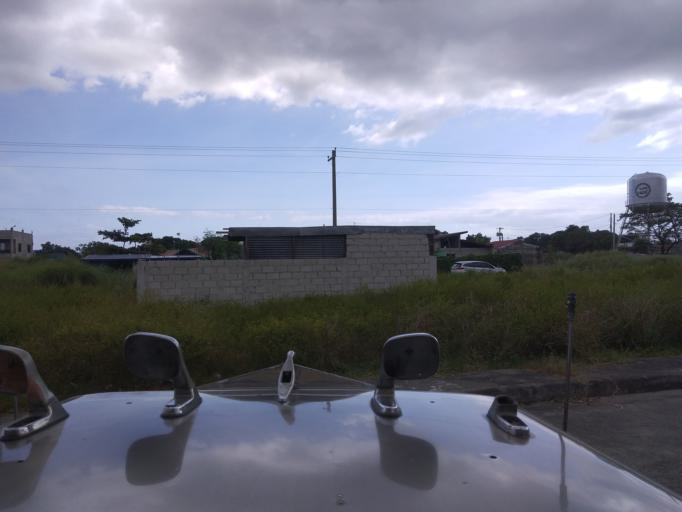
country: PH
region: Central Luzon
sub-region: Province of Pampanga
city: Pandacaqui
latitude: 15.1882
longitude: 120.6508
